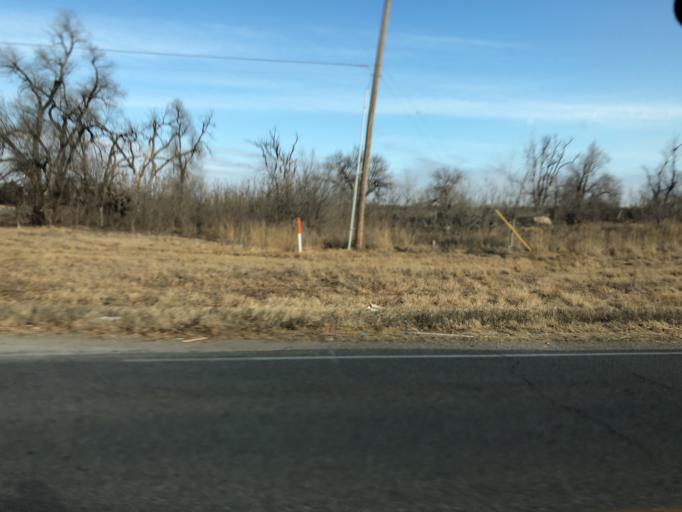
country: US
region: Kansas
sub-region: Reno County
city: South Hutchinson
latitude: 38.0573
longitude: -97.9774
